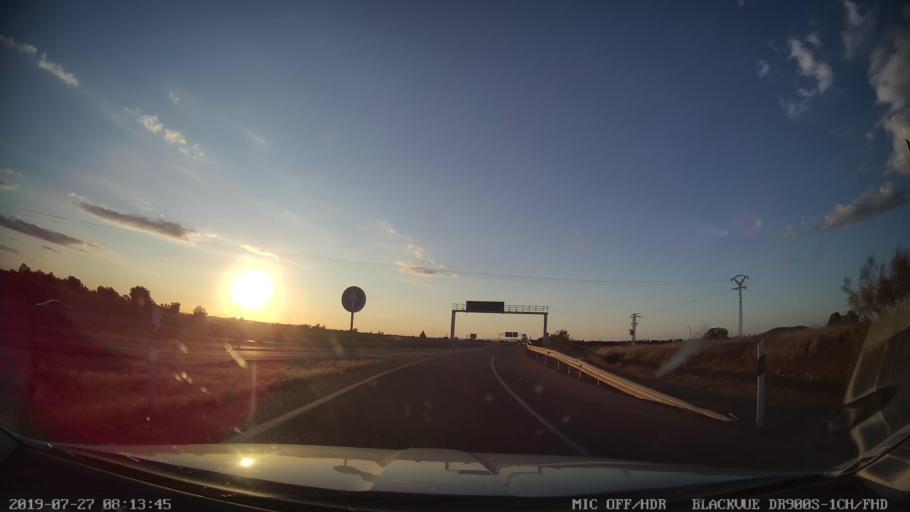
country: ES
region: Extremadura
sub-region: Provincia de Badajoz
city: Calamonte
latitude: 38.9027
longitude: -6.3708
